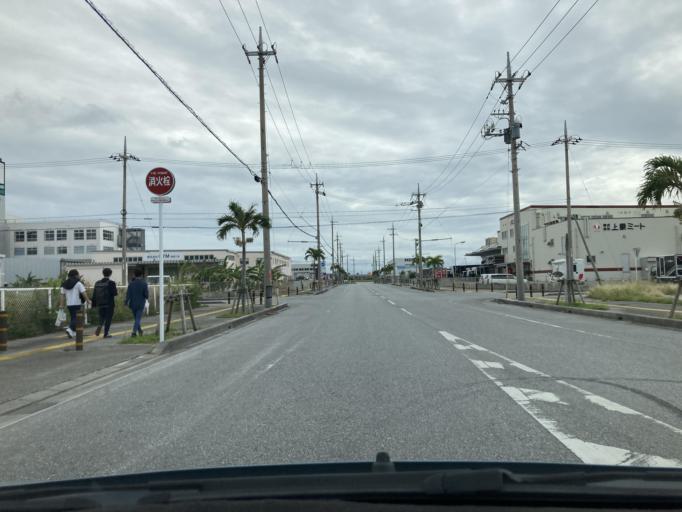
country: JP
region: Okinawa
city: Itoman
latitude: 26.1554
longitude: 127.6531
